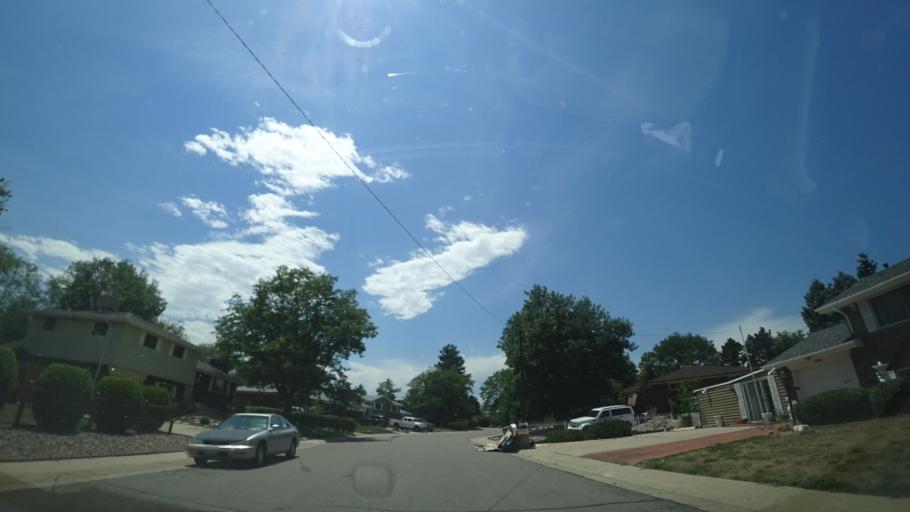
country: US
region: Colorado
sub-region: Jefferson County
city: Lakewood
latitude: 39.6912
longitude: -105.0962
